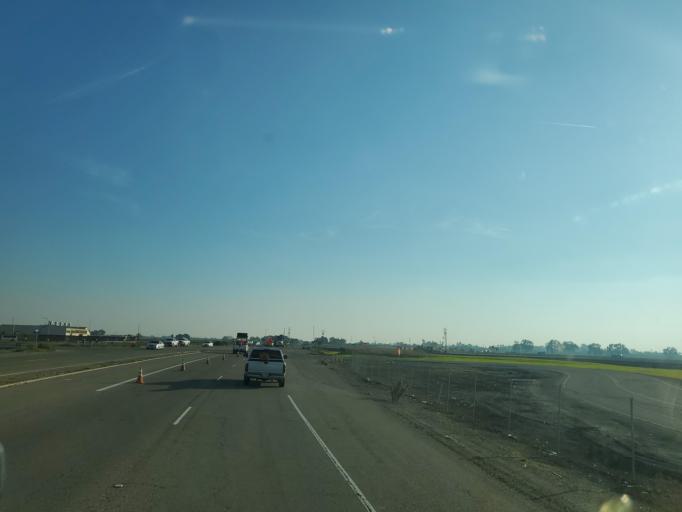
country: US
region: California
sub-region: San Joaquin County
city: French Camp
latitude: 37.8867
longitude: -121.2489
